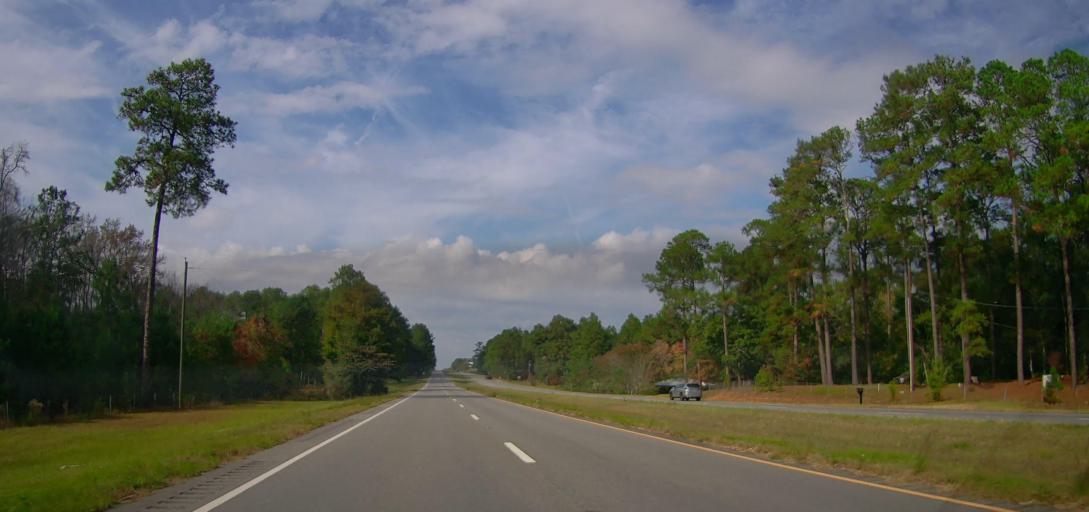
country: US
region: Georgia
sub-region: Thomas County
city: Meigs
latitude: 30.9679
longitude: -84.0329
